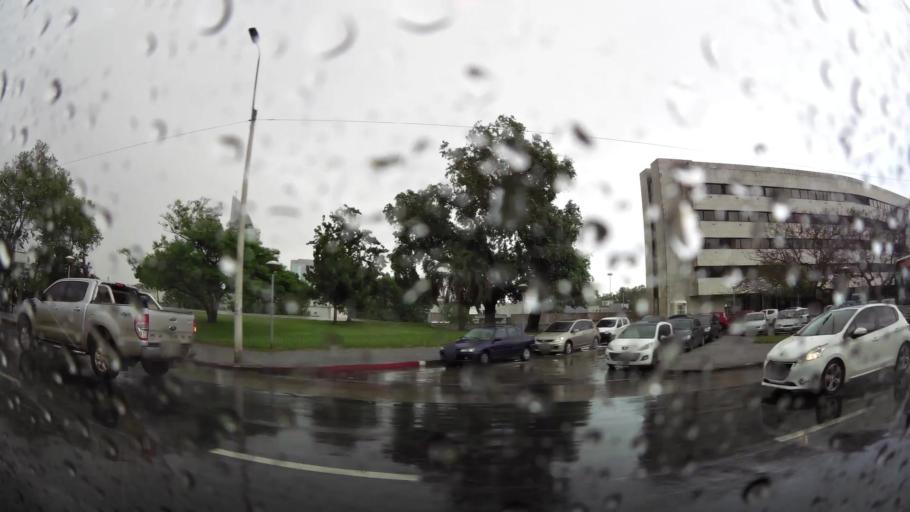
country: UY
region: Montevideo
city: Montevideo
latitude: -34.8915
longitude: -56.1885
